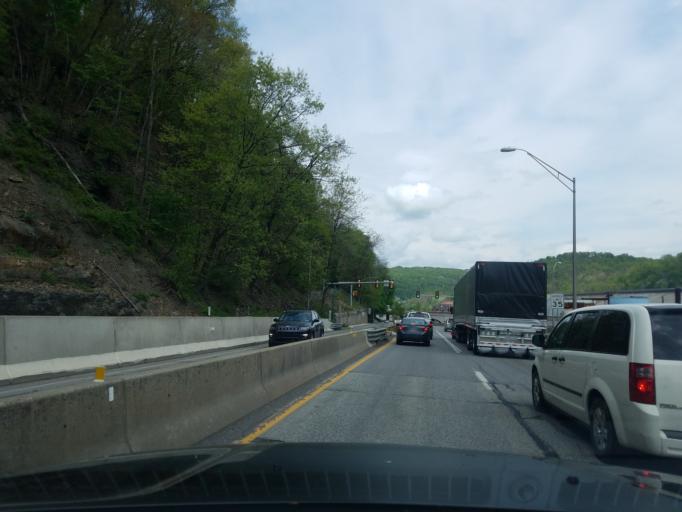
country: US
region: Pennsylvania
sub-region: Cambria County
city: Johnstown
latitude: 40.3300
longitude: -78.9261
